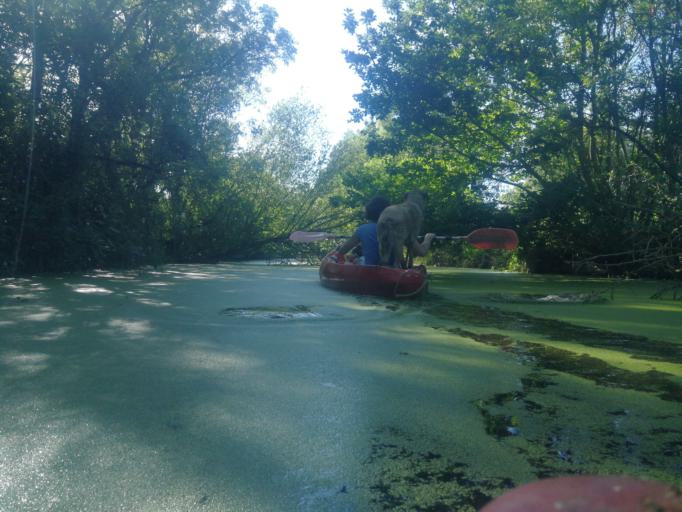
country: FR
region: Poitou-Charentes
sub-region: Departement de la Charente-Maritime
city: Marans
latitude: 46.3608
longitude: -0.9536
